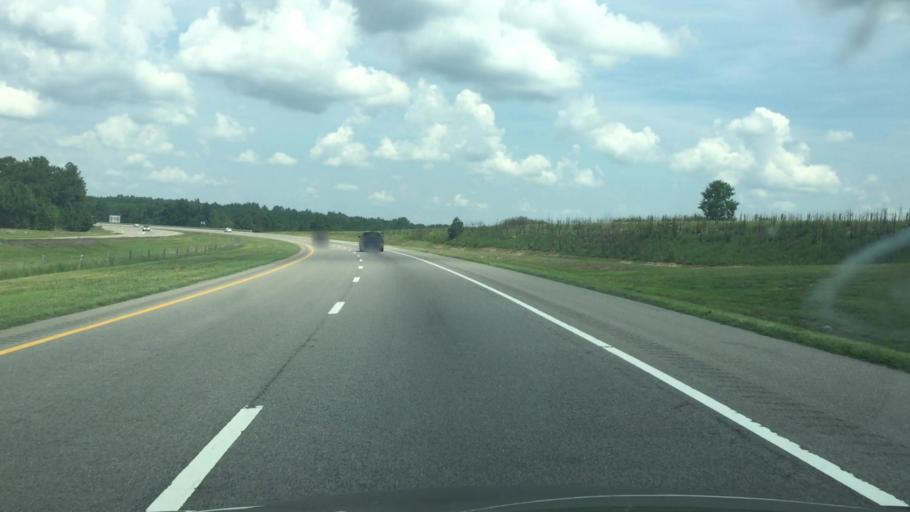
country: US
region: North Carolina
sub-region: Richmond County
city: Ellerbe
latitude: 35.1752
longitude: -79.7130
